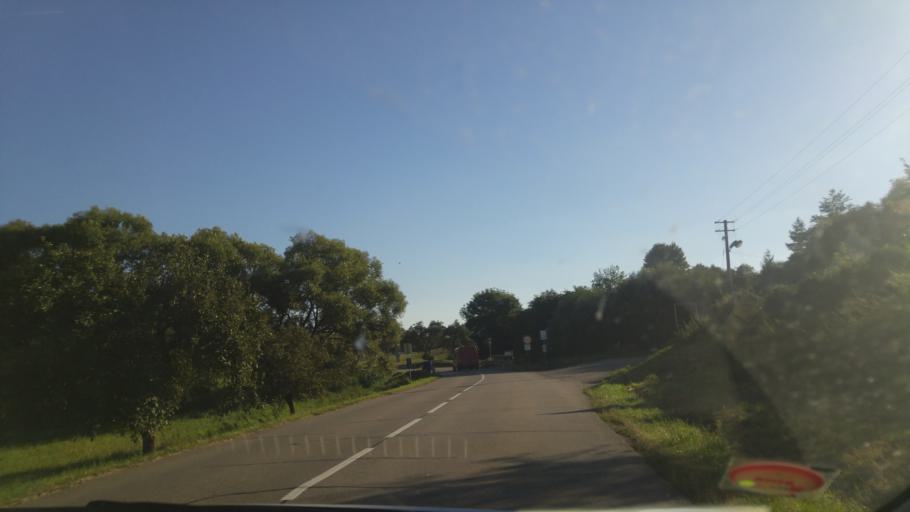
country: CZ
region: South Moravian
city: Veverska Bityska
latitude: 49.2454
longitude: 16.4464
